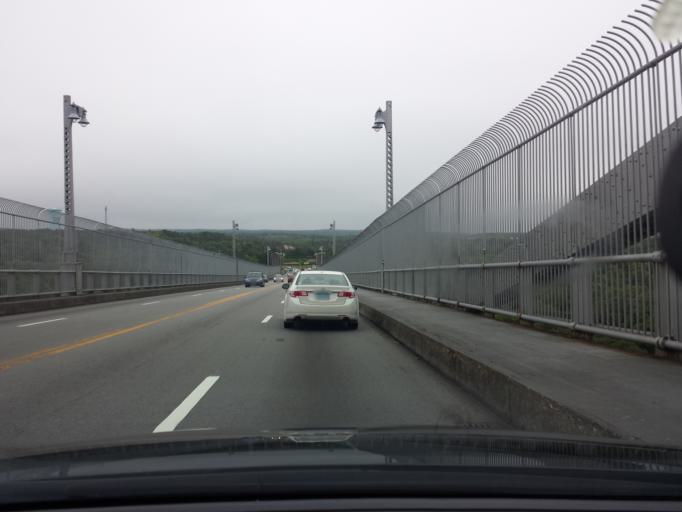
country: US
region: Massachusetts
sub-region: Barnstable County
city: Bourne
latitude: 41.7468
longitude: -70.5890
